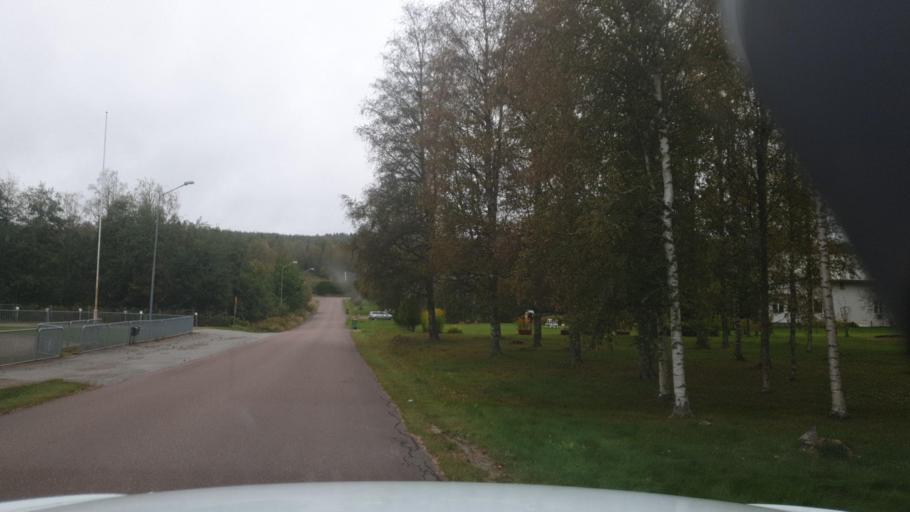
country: SE
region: Vaermland
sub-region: Arjangs Kommun
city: Arjaeng
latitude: 59.5567
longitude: 12.1226
